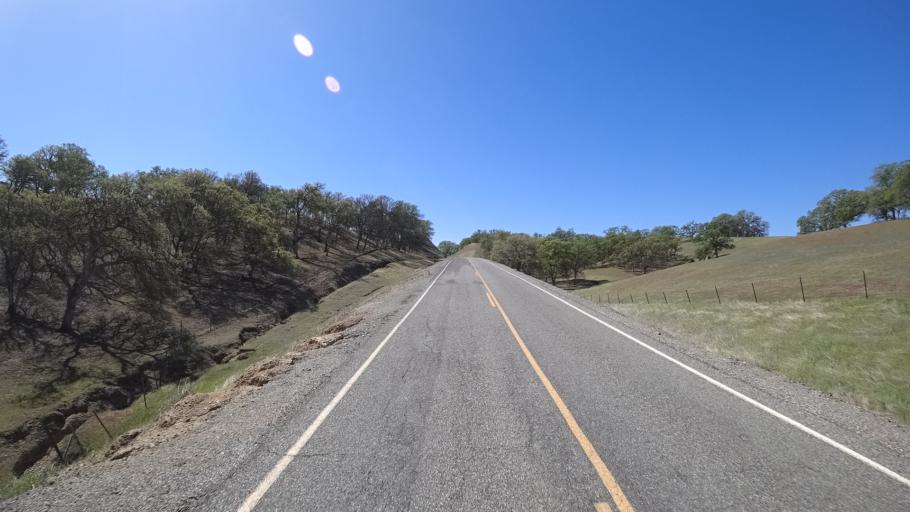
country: US
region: California
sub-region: Tehama County
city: Rancho Tehama Reserve
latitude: 39.8213
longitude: -122.3812
